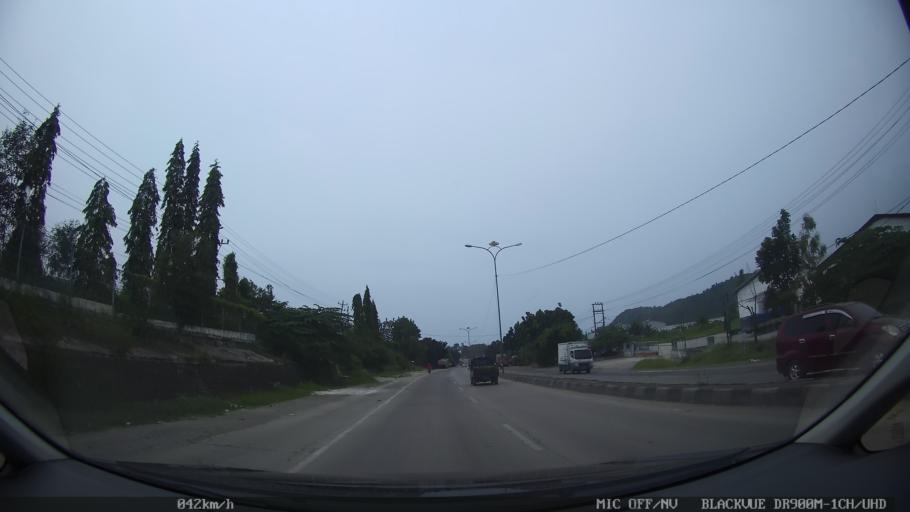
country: ID
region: Lampung
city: Bandarlampung
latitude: -5.4162
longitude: 105.2959
